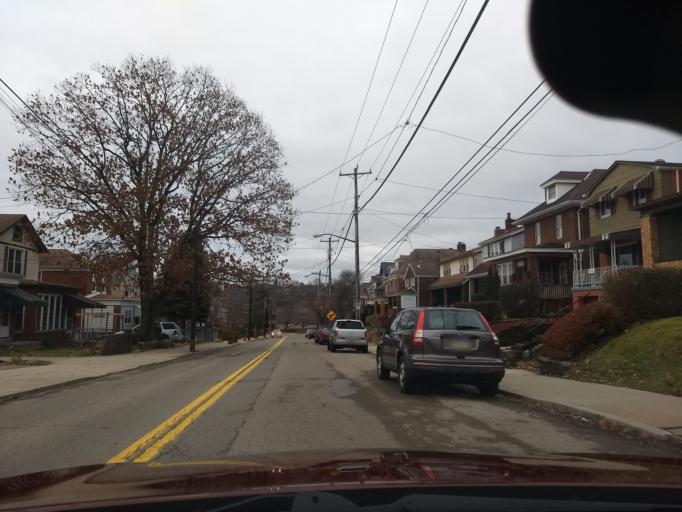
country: US
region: Pennsylvania
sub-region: Allegheny County
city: Homestead
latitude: 40.4234
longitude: -79.9315
